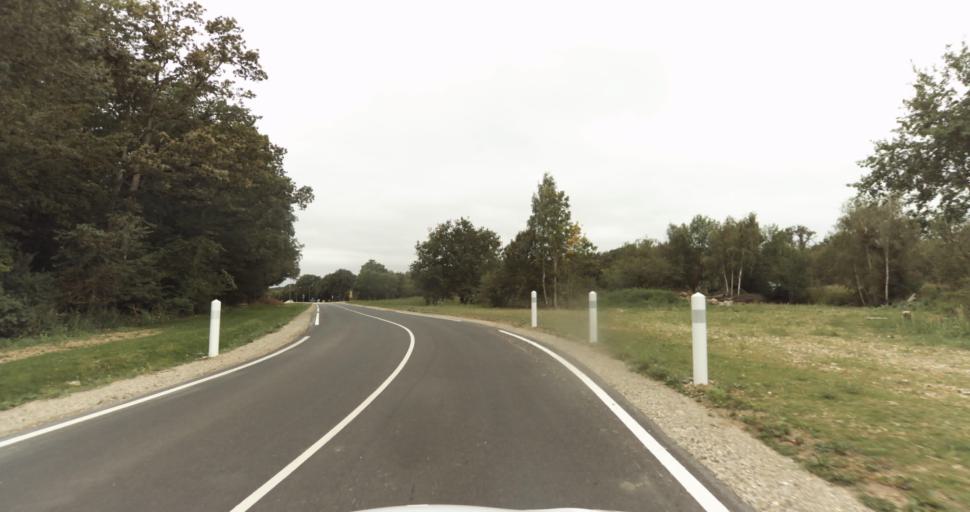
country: FR
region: Haute-Normandie
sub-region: Departement de l'Eure
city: Gravigny
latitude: 49.0344
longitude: 1.1793
